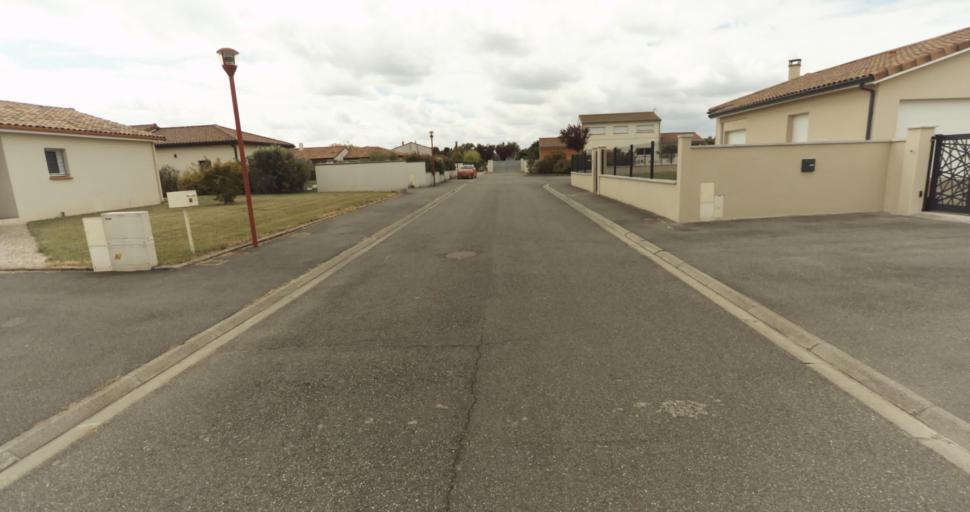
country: FR
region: Midi-Pyrenees
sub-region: Departement de la Haute-Garonne
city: Fontenilles
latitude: 43.5565
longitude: 1.1961
